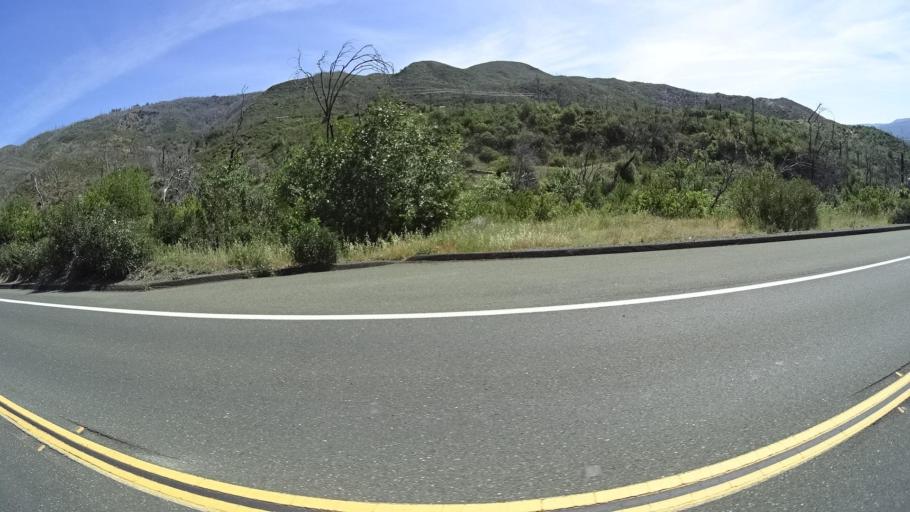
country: US
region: California
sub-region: Lake County
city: Cobb
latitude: 38.7895
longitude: -122.6949
